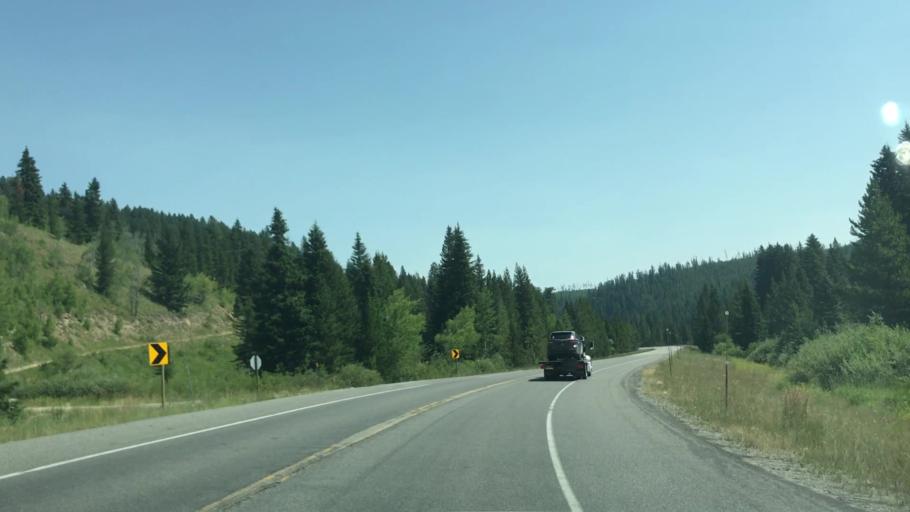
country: US
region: Montana
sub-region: Gallatin County
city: West Yellowstone
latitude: 44.8048
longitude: -111.1071
